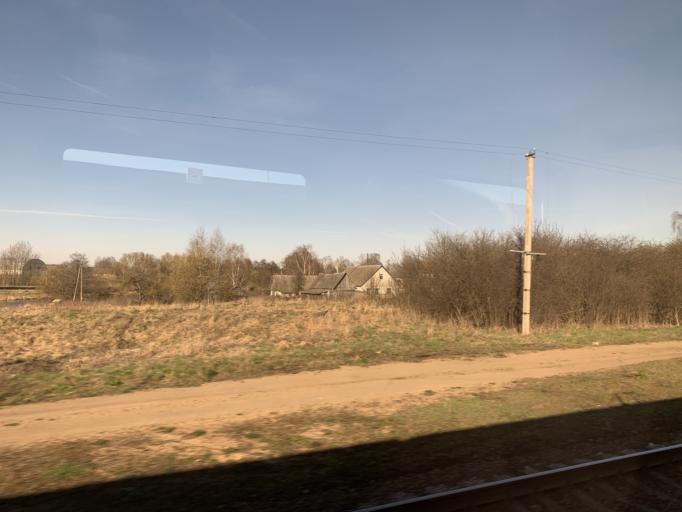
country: BY
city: Soly
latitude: 54.5330
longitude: 26.0769
